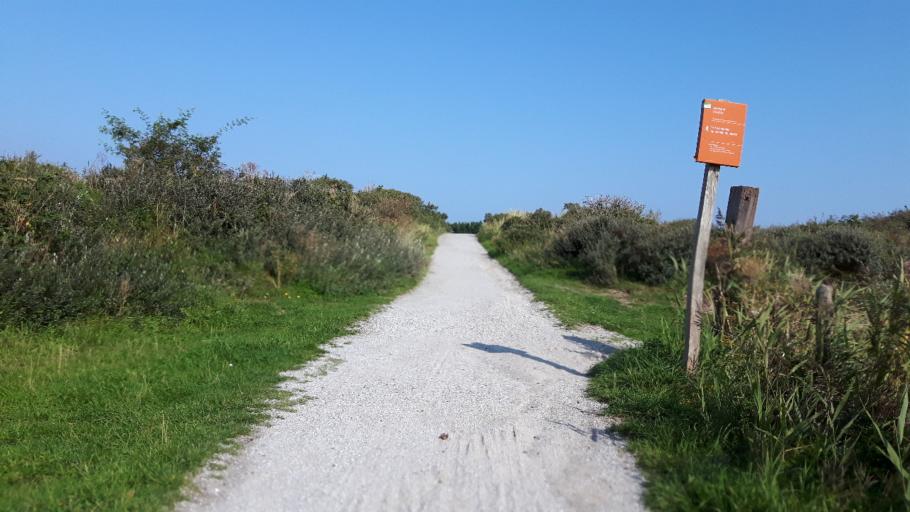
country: NL
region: Friesland
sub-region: Gemeente Ameland
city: Nes
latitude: 53.4572
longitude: 5.8147
